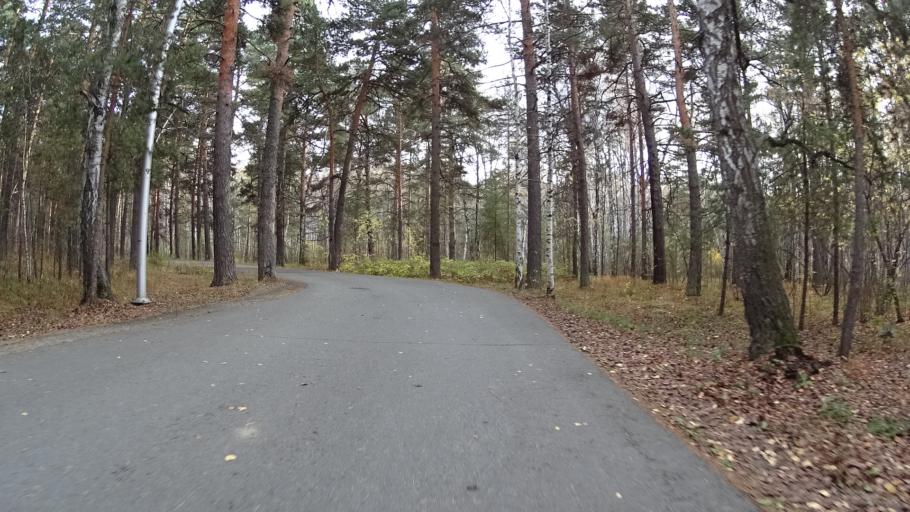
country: RU
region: Chelyabinsk
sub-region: Gorod Chelyabinsk
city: Chelyabinsk
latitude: 55.1403
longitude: 61.3490
